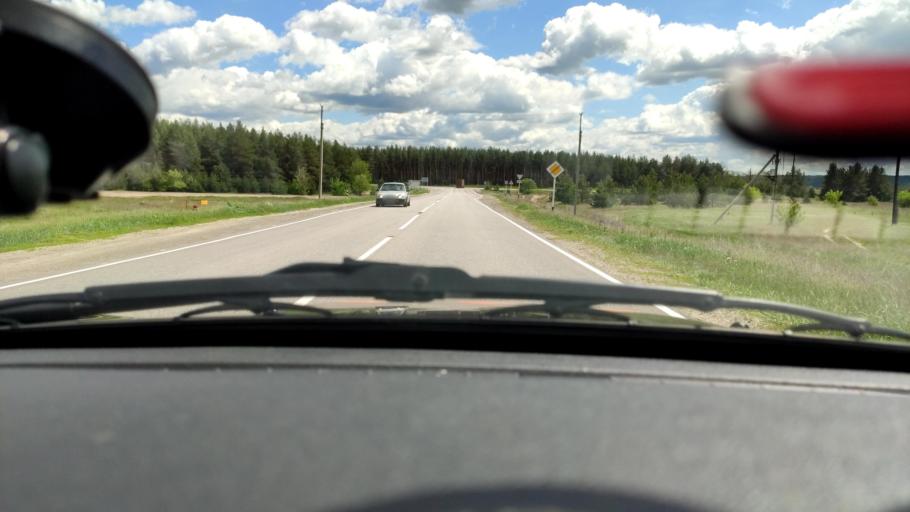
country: RU
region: Voronezj
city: Uryv-Pokrovka
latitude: 51.0501
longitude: 38.9793
